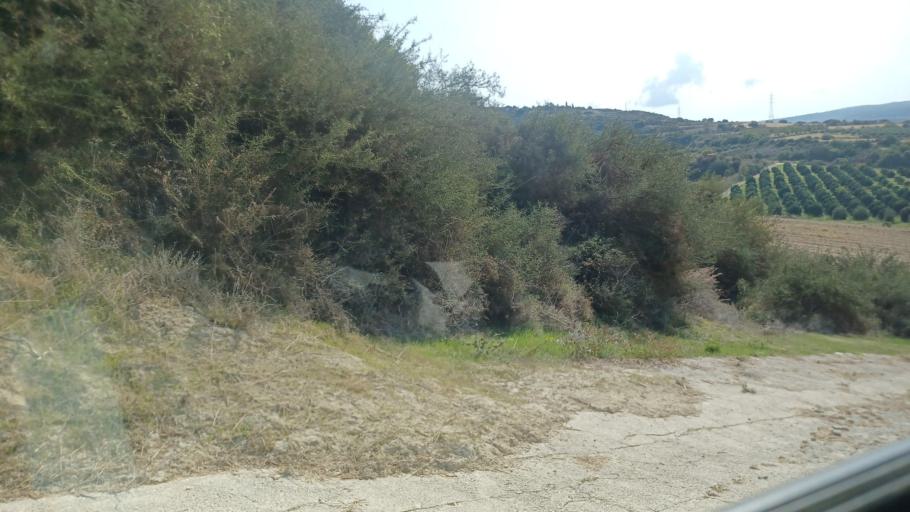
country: CY
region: Pafos
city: Polis
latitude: 34.9992
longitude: 32.4556
